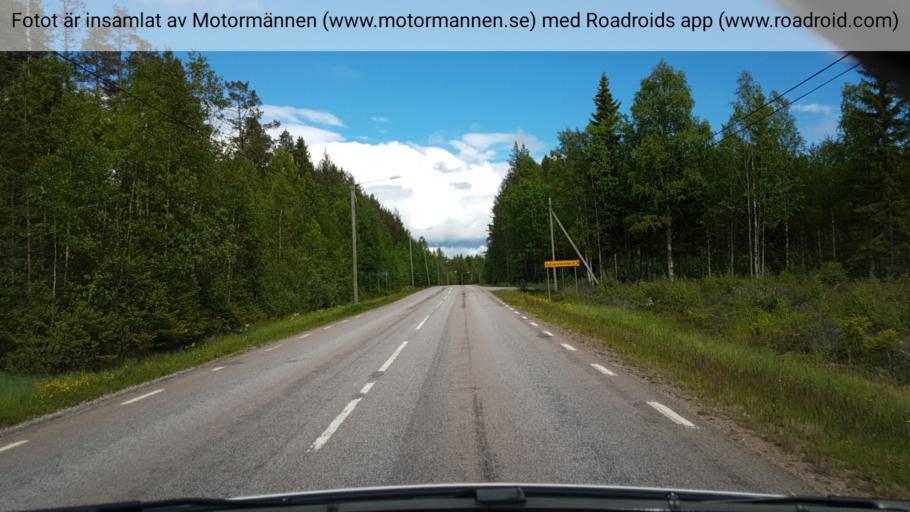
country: SE
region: Vaesterbotten
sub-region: Umea Kommun
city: Hoernefors
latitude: 63.6177
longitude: 19.8867
